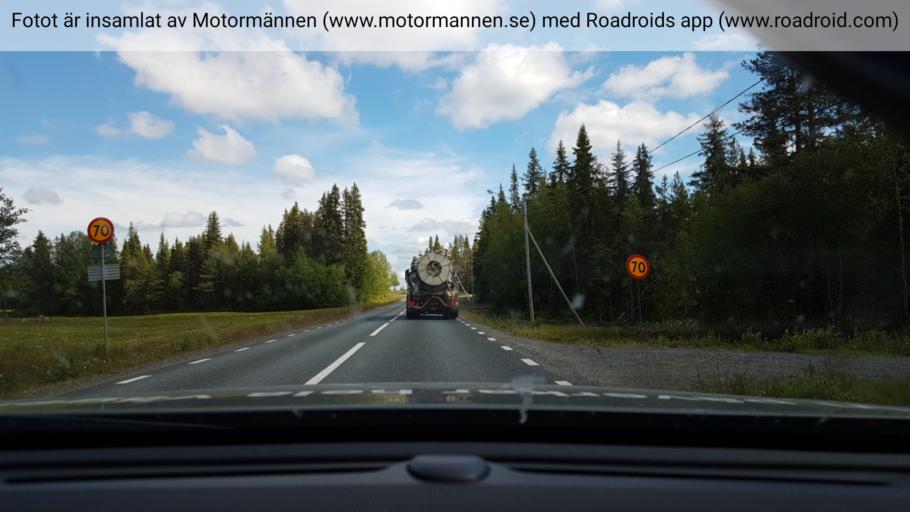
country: SE
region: Vaesterbotten
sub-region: Sorsele Kommun
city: Sorsele
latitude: 65.5576
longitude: 17.8423
